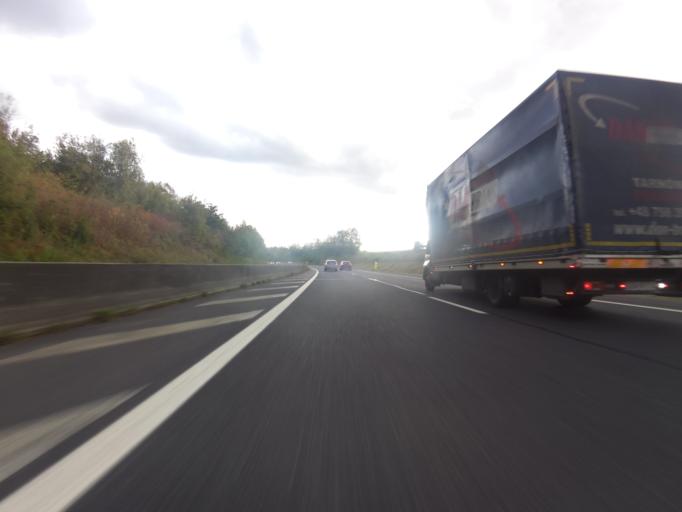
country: FR
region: Haute-Normandie
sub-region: Departement de la Seine-Maritime
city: Saint-Saens
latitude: 49.6481
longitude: 1.2653
